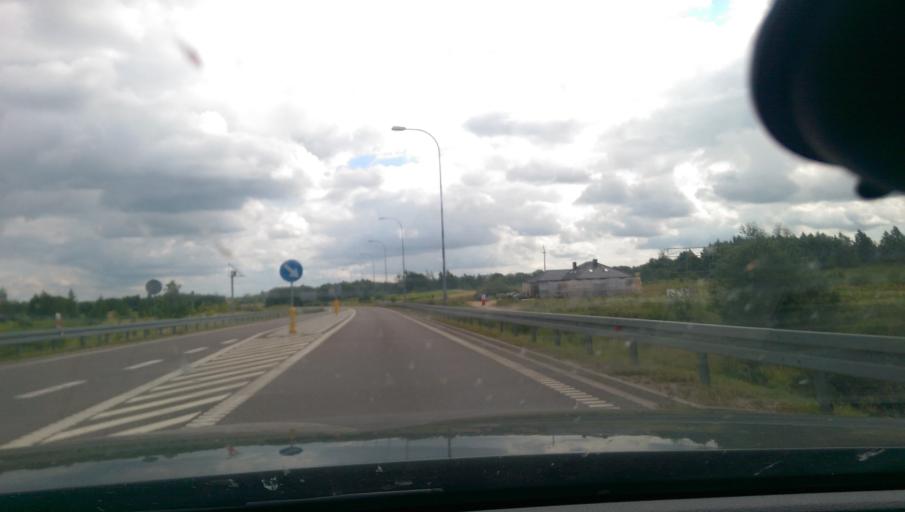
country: PL
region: Warmian-Masurian Voivodeship
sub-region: Powiat goldapski
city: Goldap
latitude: 54.2978
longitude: 22.2984
